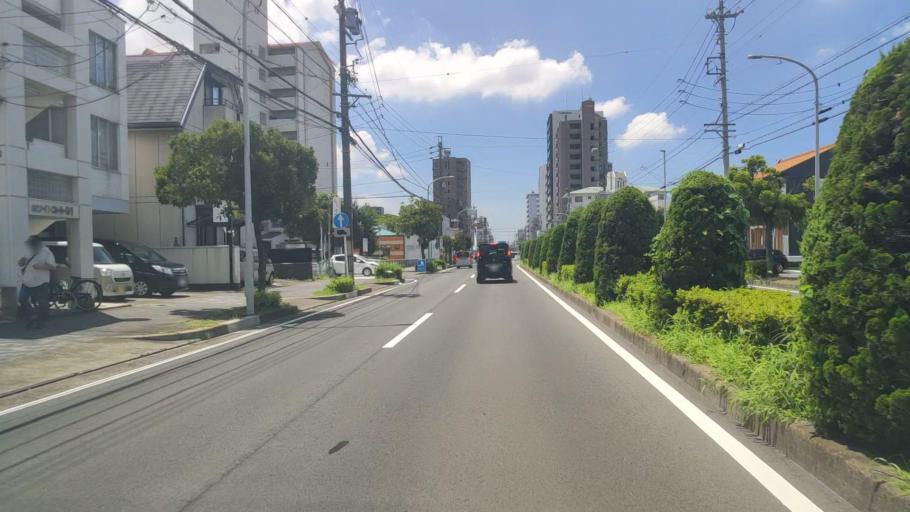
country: JP
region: Aichi
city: Kanie
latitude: 35.1443
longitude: 136.8532
